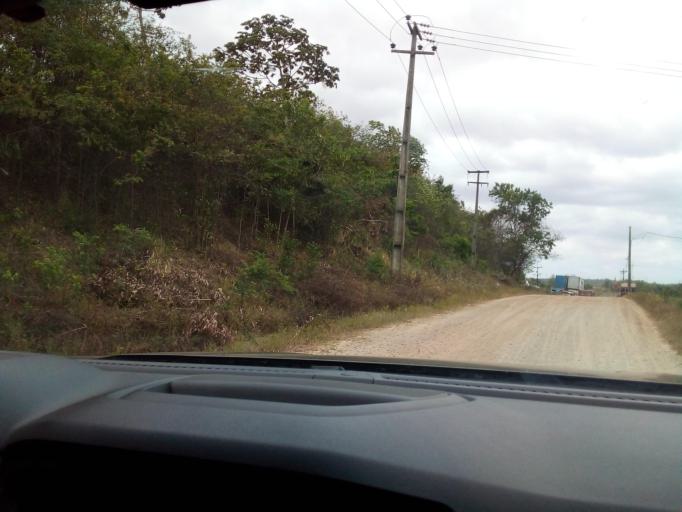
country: BR
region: Maranhao
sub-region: Sao Luis
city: Sao Luis
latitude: -2.6729
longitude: -44.2954
